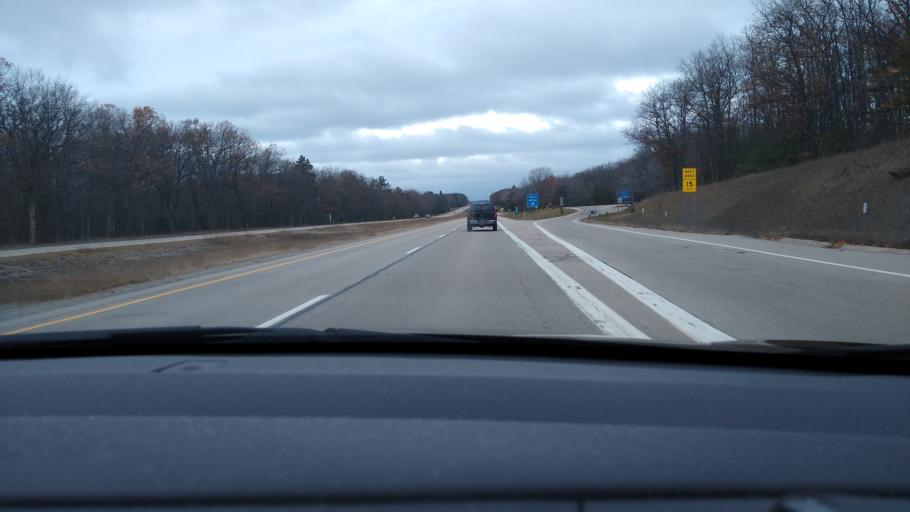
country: US
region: Michigan
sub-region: Cheboygan County
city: Indian River
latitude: 45.5013
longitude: -84.6155
